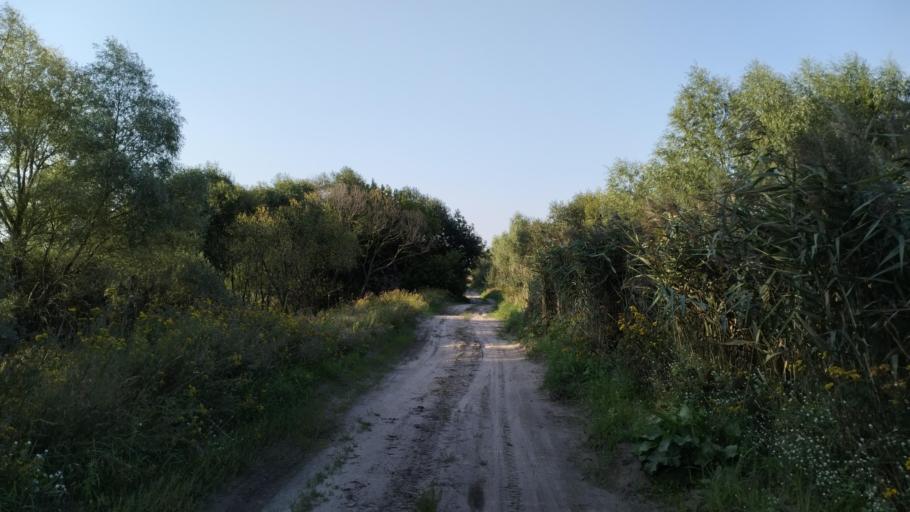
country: BY
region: Brest
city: Davyd-Haradok
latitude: 52.0283
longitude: 27.1947
